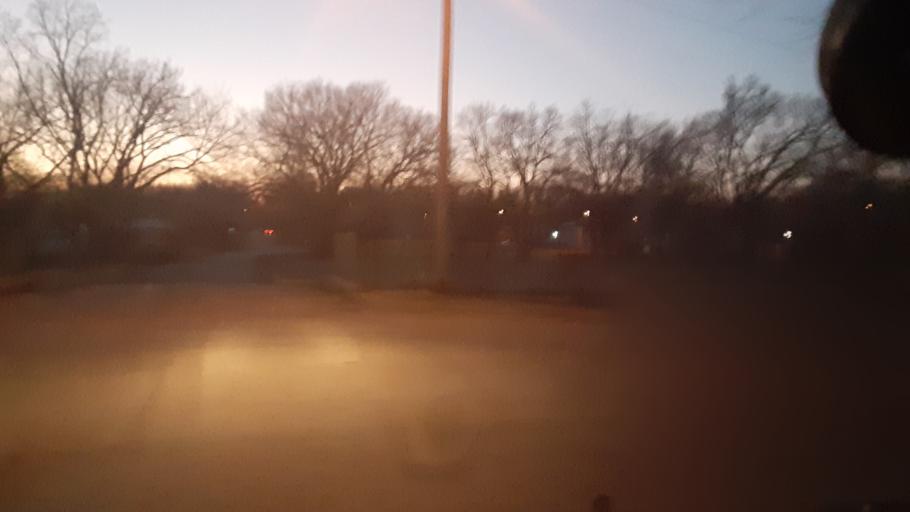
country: US
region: Oklahoma
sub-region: Payne County
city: Stillwater
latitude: 36.1113
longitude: -97.0680
